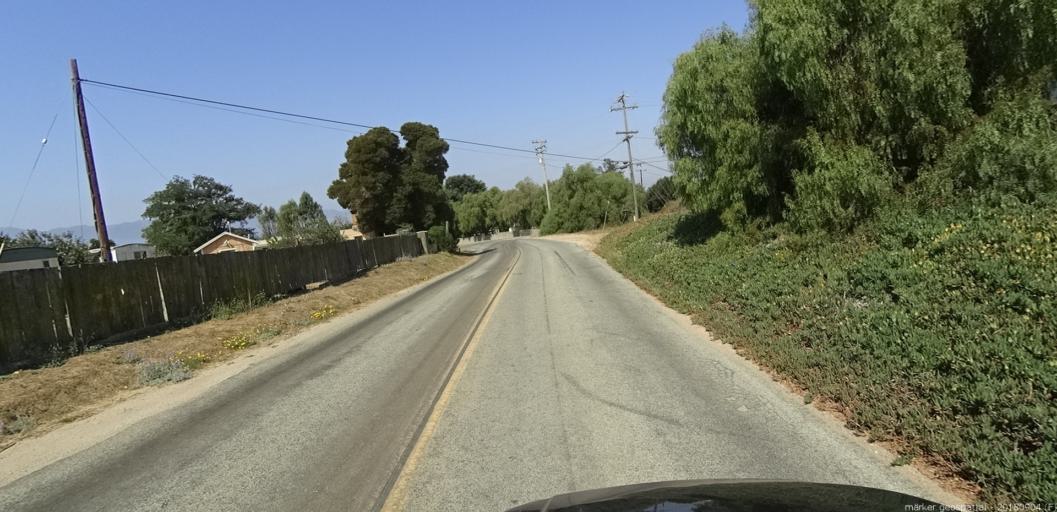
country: US
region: California
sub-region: Monterey County
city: Gonzales
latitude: 36.5039
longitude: -121.3823
